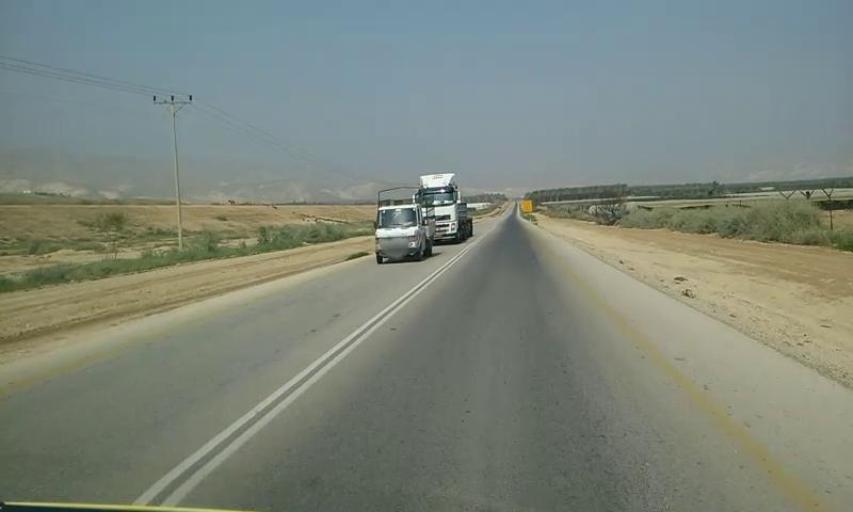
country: PS
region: West Bank
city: Al `Awja
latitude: 31.9869
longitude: 35.4618
